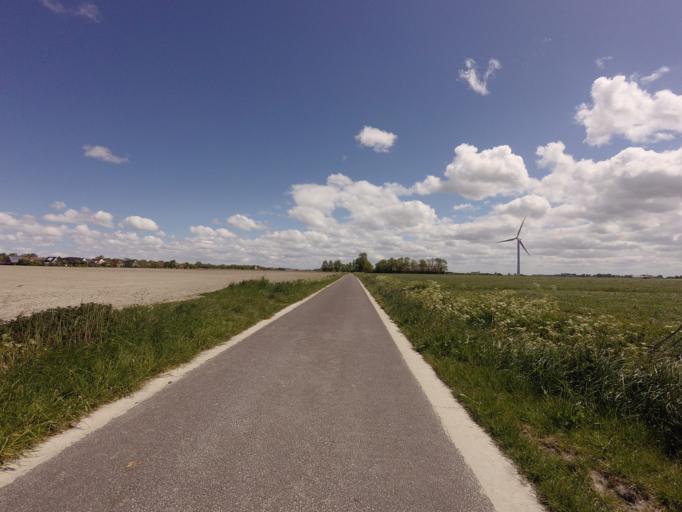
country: NL
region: Friesland
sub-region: Gemeente Harlingen
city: Harlingen
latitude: 53.1374
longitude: 5.4295
